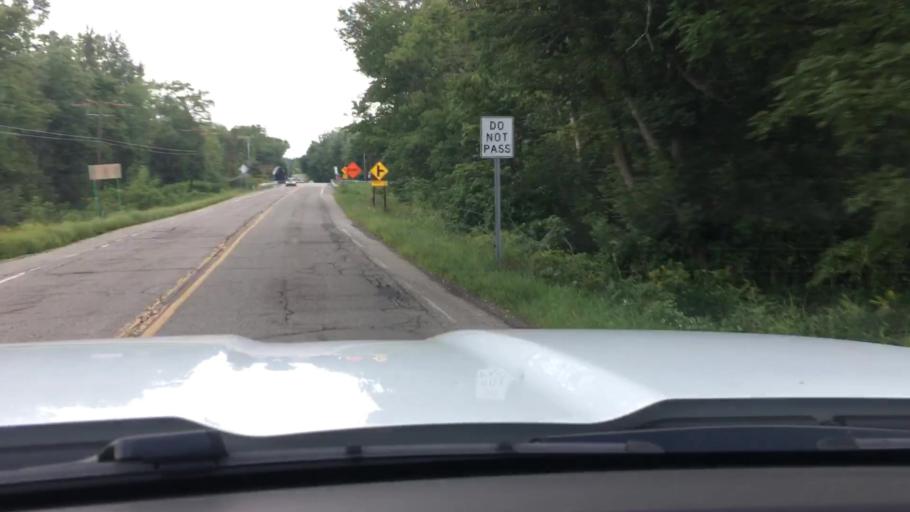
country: US
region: Michigan
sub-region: Eaton County
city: Dimondale
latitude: 42.5823
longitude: -84.6036
